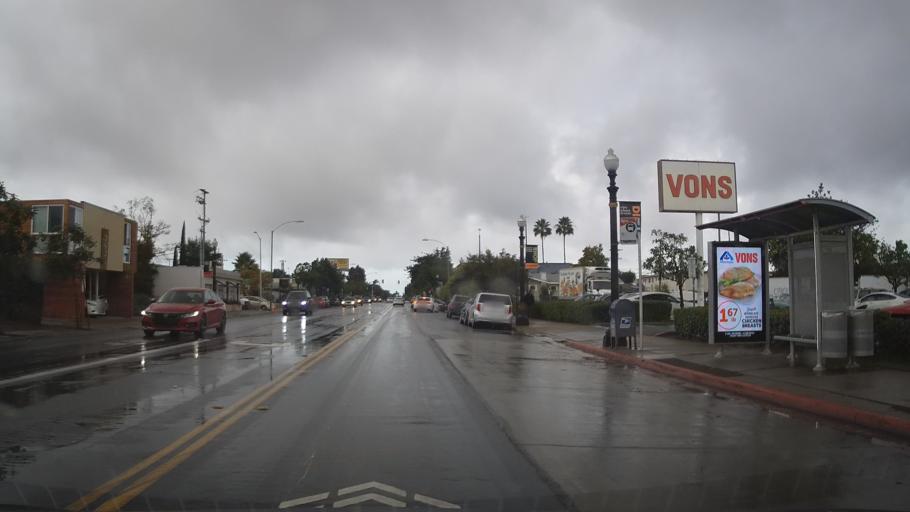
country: US
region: California
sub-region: San Diego County
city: San Diego
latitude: 32.7634
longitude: -117.1141
